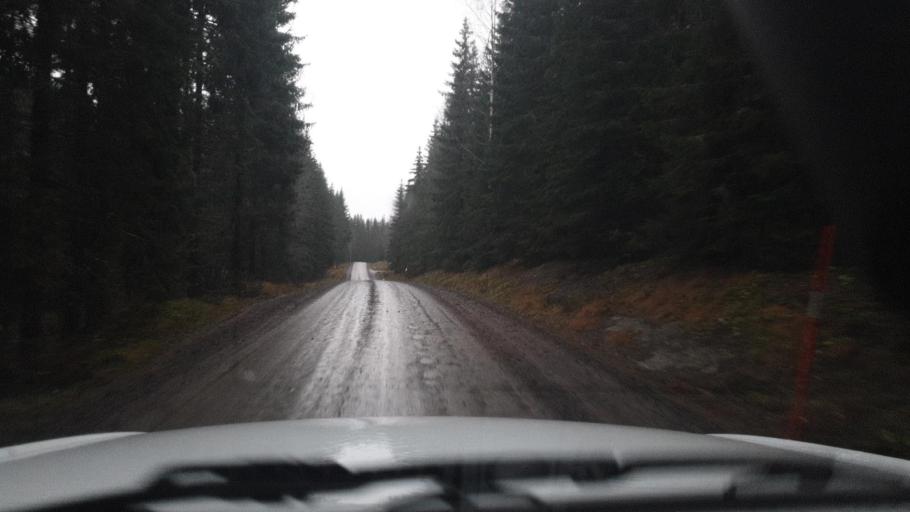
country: SE
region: Vaermland
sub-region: Arvika Kommun
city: Arvika
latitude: 59.9569
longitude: 12.6599
